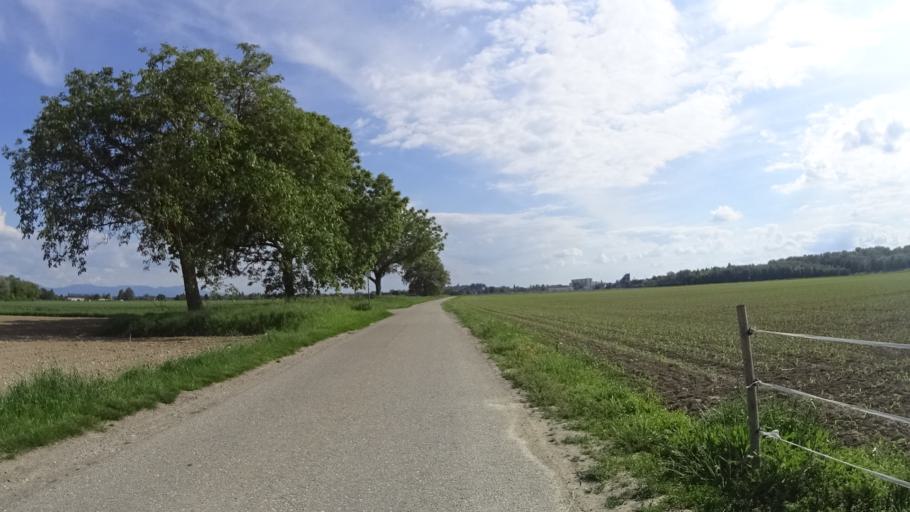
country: DE
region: Baden-Wuerttemberg
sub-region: Freiburg Region
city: Breisach am Rhein
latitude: 48.0563
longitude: 7.5874
